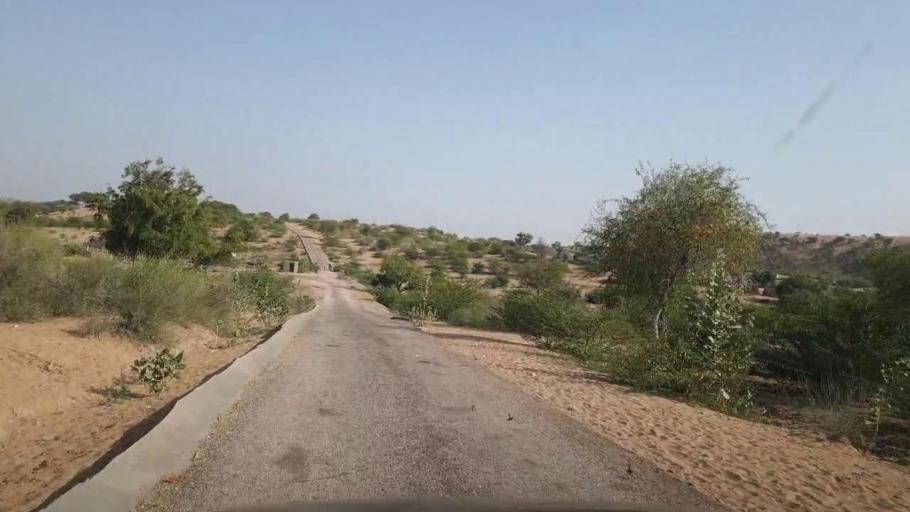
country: PK
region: Sindh
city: Islamkot
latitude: 25.1245
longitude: 70.5067
